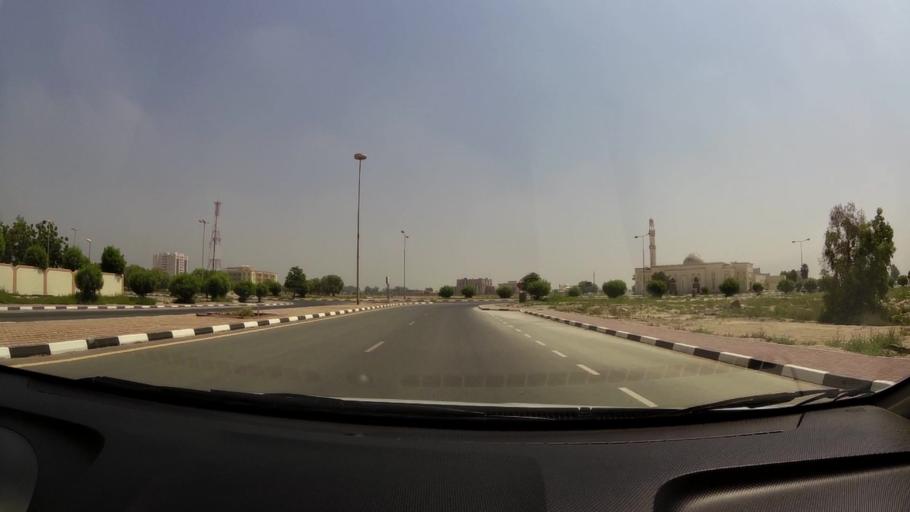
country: AE
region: Umm al Qaywayn
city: Umm al Qaywayn
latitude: 25.5734
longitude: 55.5623
